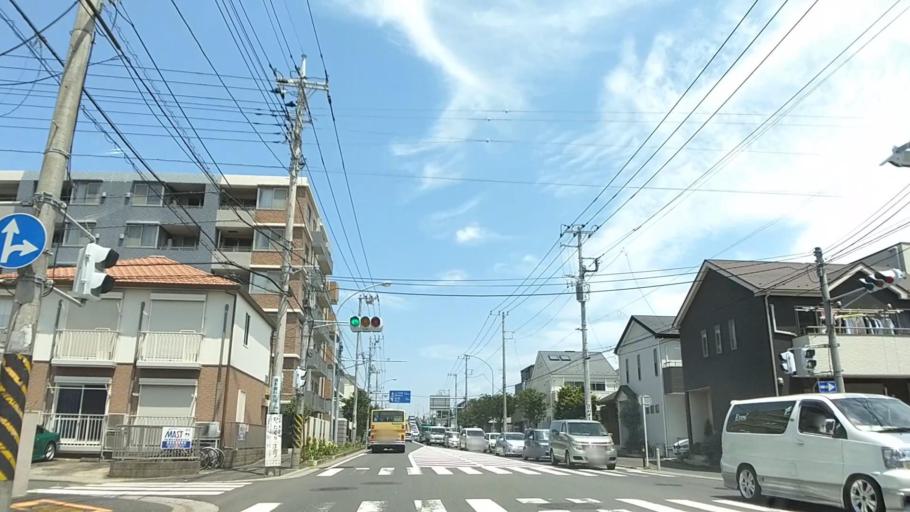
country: JP
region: Kanagawa
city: Minami-rinkan
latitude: 35.4670
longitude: 139.4801
